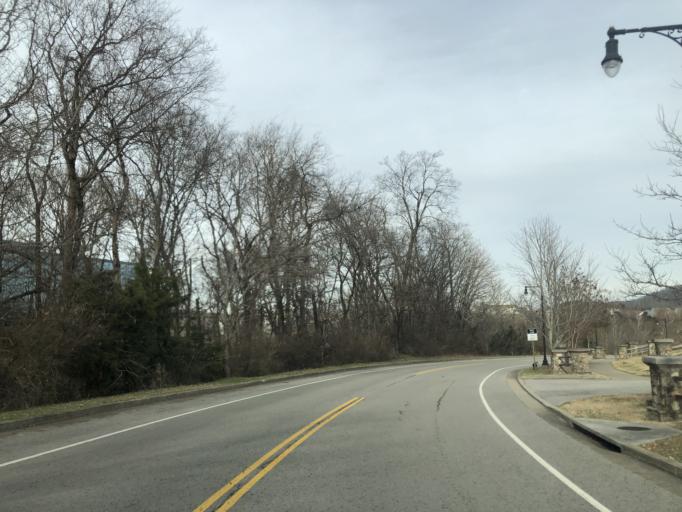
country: US
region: Tennessee
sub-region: Williamson County
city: Franklin
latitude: 35.9295
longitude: -86.8033
